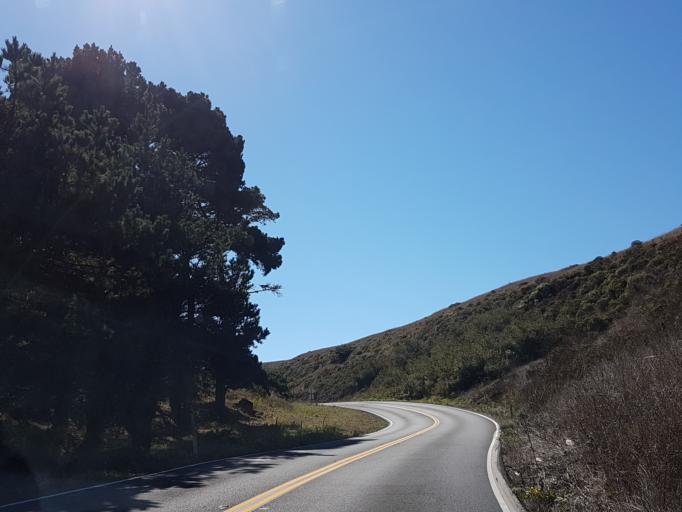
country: US
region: California
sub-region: Sonoma County
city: Sea Ranch
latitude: 38.9035
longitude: -123.6914
